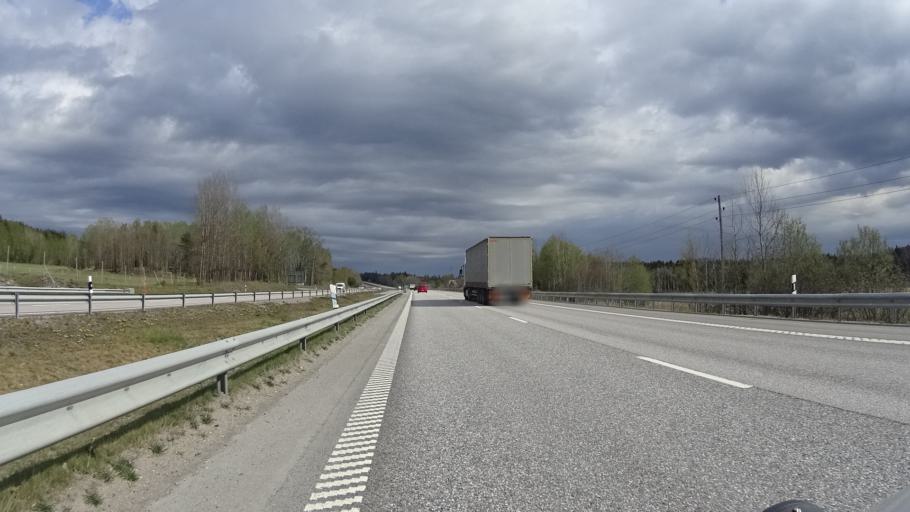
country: SE
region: Stockholm
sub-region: Nykvarns Kommun
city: Nykvarn
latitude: 59.1876
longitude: 17.4754
